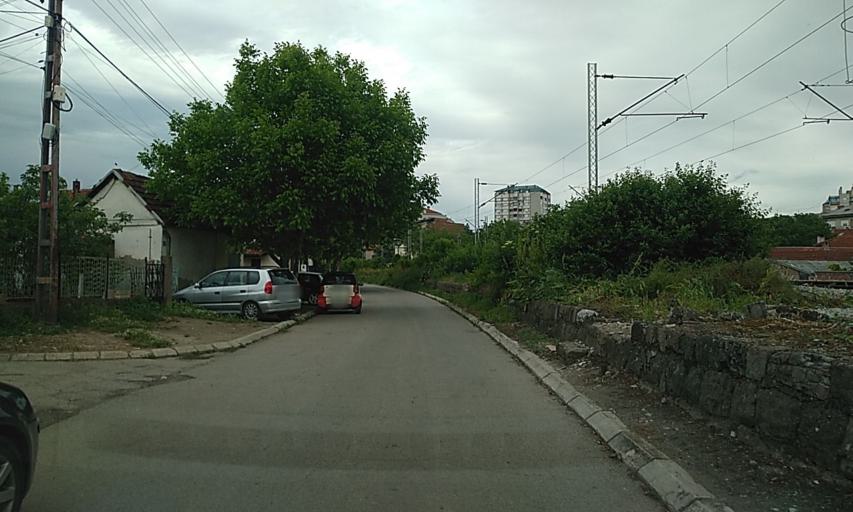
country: RS
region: Central Serbia
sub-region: Nisavski Okrug
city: Nis
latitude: 43.3174
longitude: 21.8846
